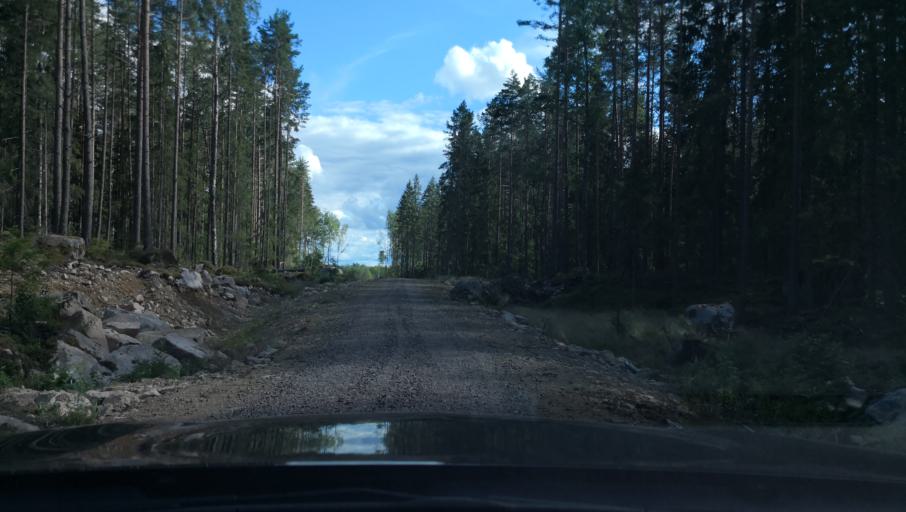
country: SE
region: Vaestmanland
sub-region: Hallstahammars Kommun
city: Hallstahammar
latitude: 59.6583
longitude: 16.2014
